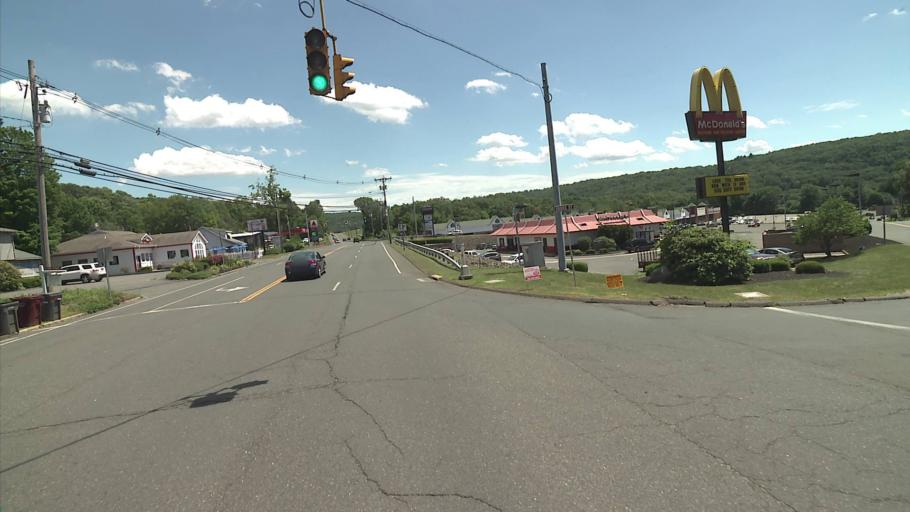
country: US
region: Connecticut
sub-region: New Haven County
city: Naugatuck
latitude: 41.4750
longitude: -73.0434
